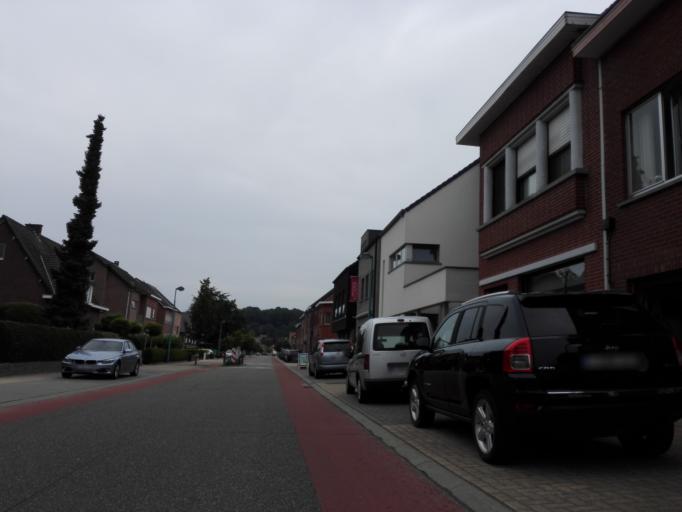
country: BE
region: Flanders
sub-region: Provincie Vlaams-Brabant
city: Holsbeek
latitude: 50.8907
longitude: 4.7683
